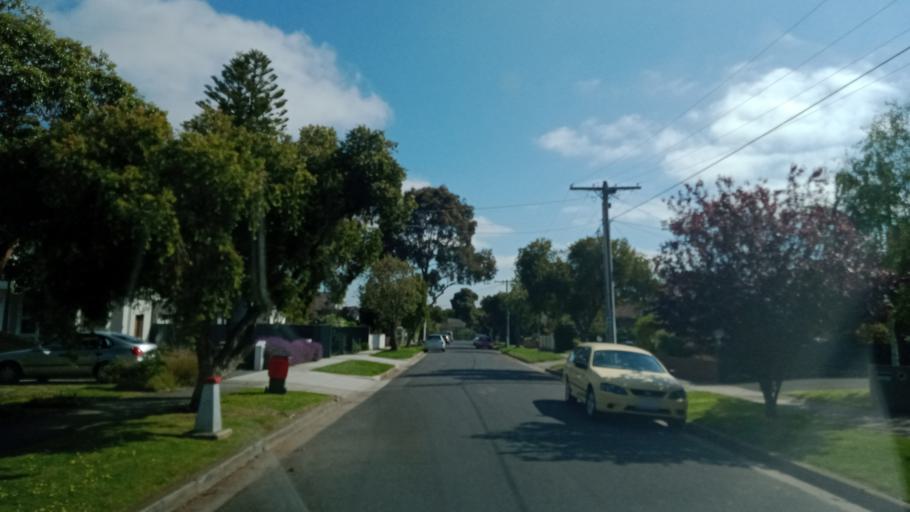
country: AU
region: Victoria
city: Hughesdale
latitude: -37.9139
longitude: 145.0782
